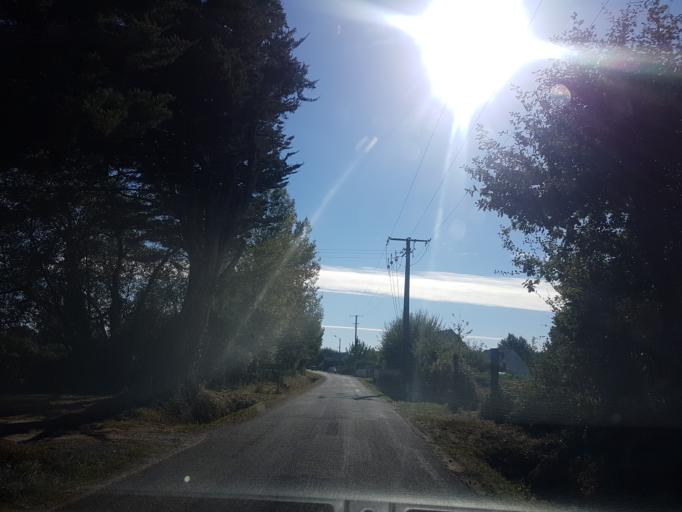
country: FR
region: Pays de la Loire
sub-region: Departement de la Loire-Atlantique
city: Petit-Mars
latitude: 47.3920
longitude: -1.4622
